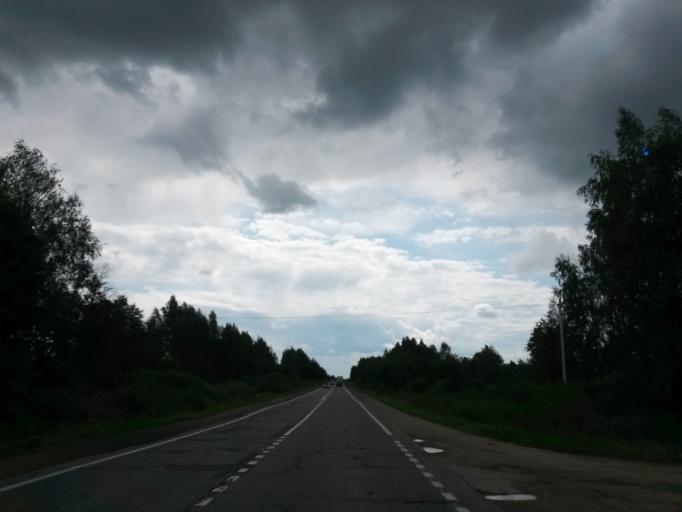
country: RU
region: Jaroslavl
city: Gavrilov-Yam
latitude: 57.3686
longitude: 39.9076
